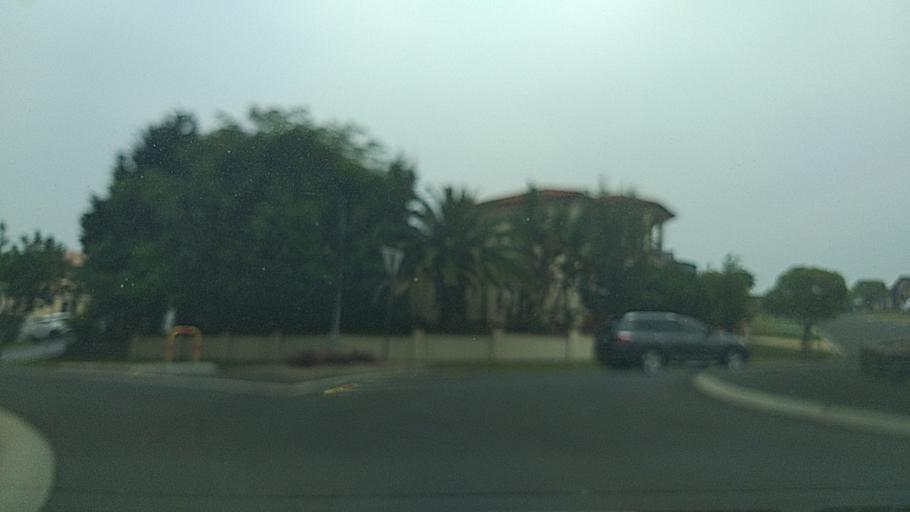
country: AU
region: New South Wales
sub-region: Shellharbour
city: Flinders
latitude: -34.5952
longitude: 150.8536
